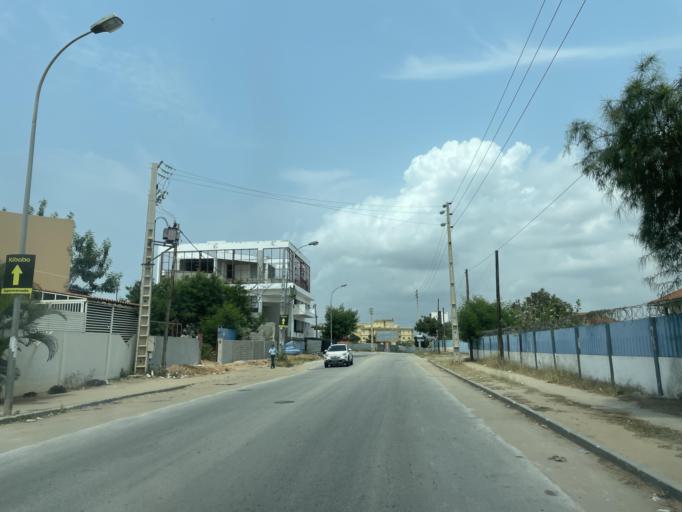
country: AO
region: Luanda
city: Luanda
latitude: -8.9234
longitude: 13.1949
